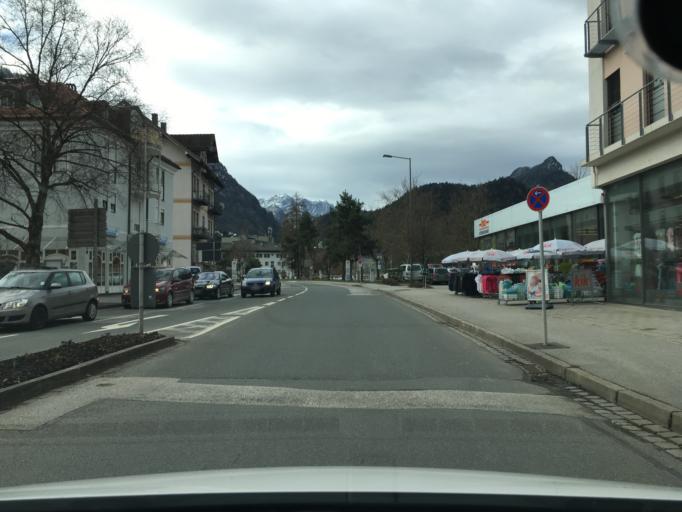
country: DE
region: Bavaria
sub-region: Upper Bavaria
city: Bad Reichenhall
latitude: 47.7263
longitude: 12.8759
